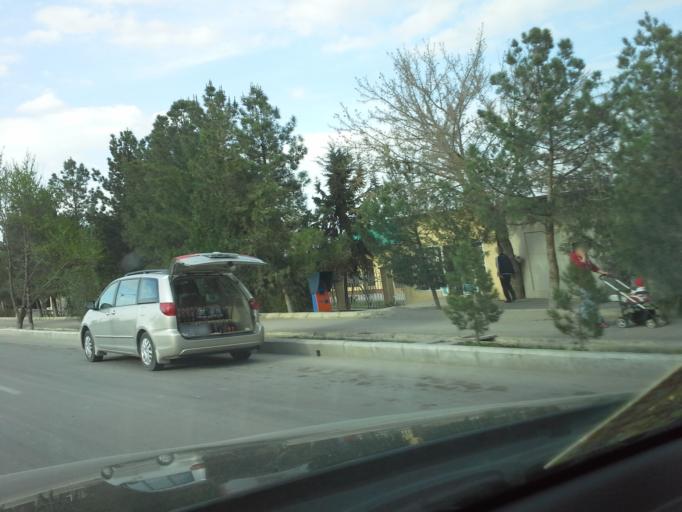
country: TM
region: Ahal
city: Abadan
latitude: 37.9615
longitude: 58.2232
